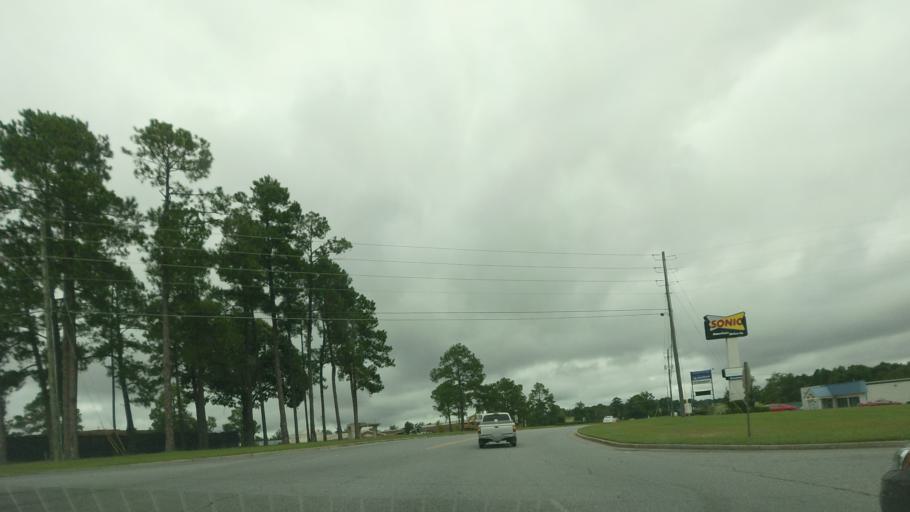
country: US
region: Georgia
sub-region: Laurens County
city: Dublin
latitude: 32.5421
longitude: -82.9465
